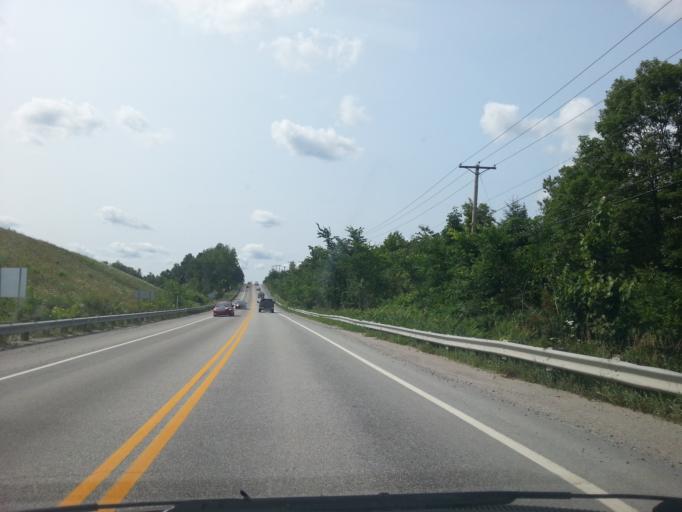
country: CA
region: Quebec
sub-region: Outaouais
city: Wakefield
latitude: 45.6135
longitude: -75.9143
